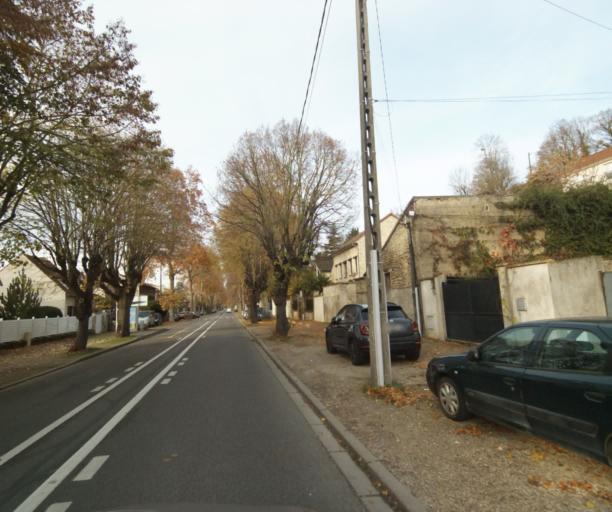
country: FR
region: Ile-de-France
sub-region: Departement des Yvelines
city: Triel-sur-Seine
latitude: 48.9867
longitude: 1.9966
